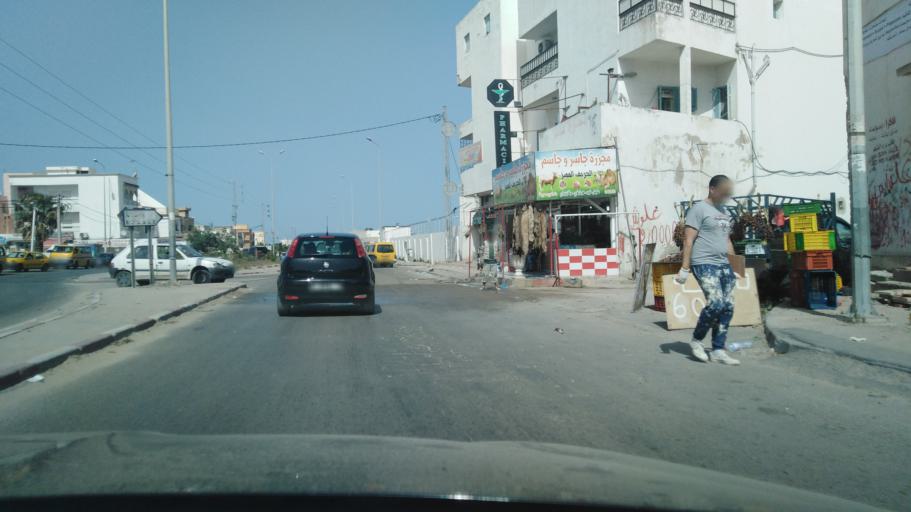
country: TN
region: Susah
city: Sousse
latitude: 35.7980
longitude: 10.6066
